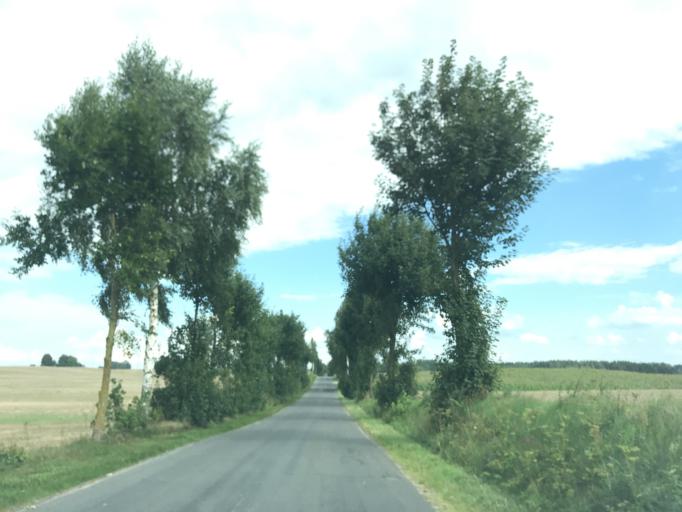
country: PL
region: Kujawsko-Pomorskie
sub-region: Powiat brodnicki
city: Brzozie
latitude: 53.3289
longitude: 19.6739
